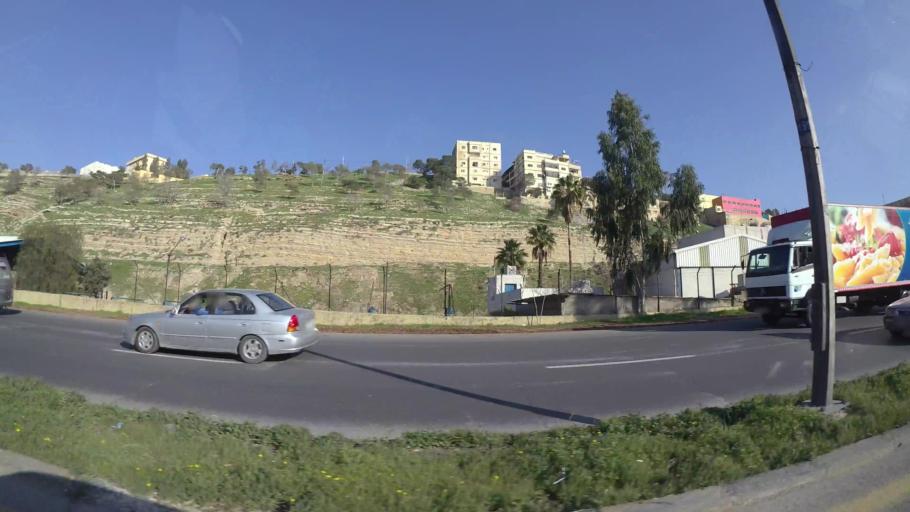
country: JO
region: Amman
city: Amman
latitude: 31.9729
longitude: 35.9713
